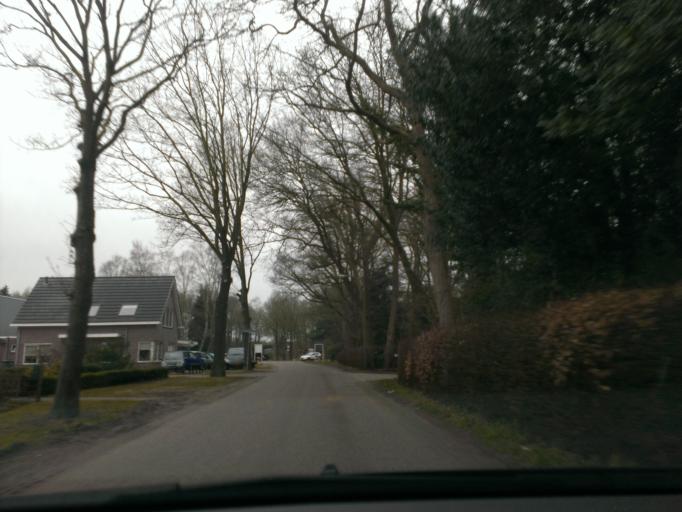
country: NL
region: Gelderland
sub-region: Gemeente Heerde
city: Heerde
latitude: 52.3857
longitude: 6.0185
